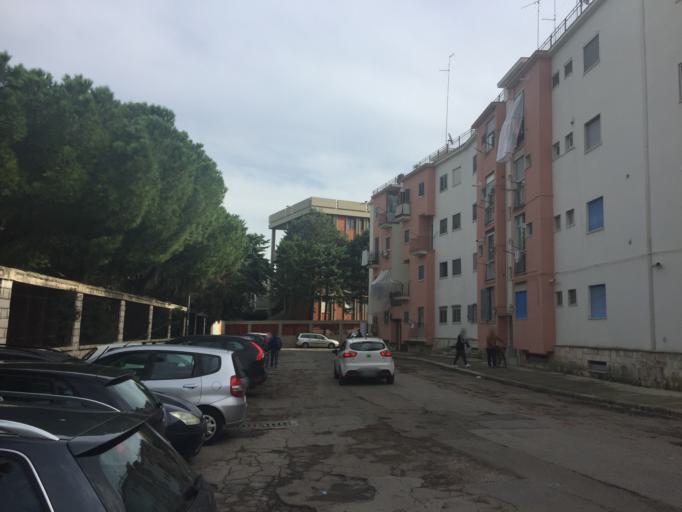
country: IT
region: Apulia
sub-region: Provincia di Bari
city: Bari
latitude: 41.1079
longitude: 16.8813
